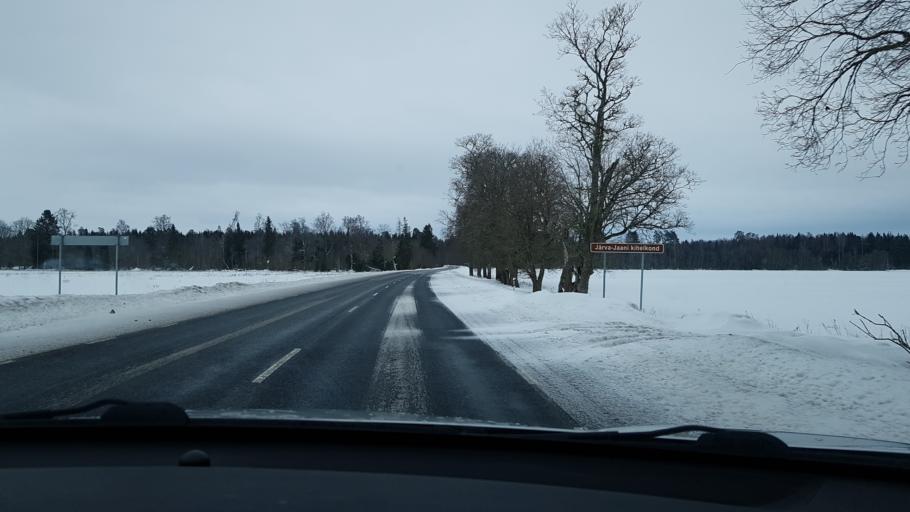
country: EE
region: Jaervamaa
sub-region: Jaerva-Jaani vald
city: Jarva-Jaani
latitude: 59.1017
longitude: 25.8149
